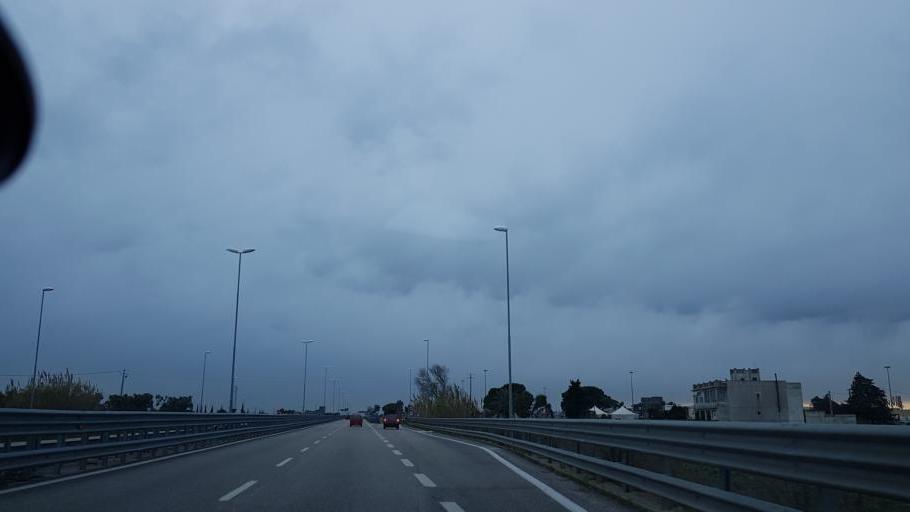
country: IT
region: Apulia
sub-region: Provincia di Brindisi
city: Brindisi
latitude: 40.6195
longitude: 17.9082
